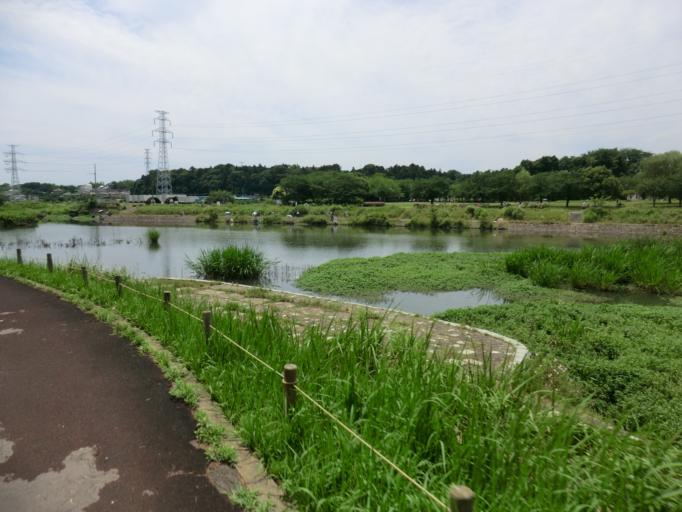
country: JP
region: Chiba
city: Kashiwa
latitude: 35.8679
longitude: 139.9897
